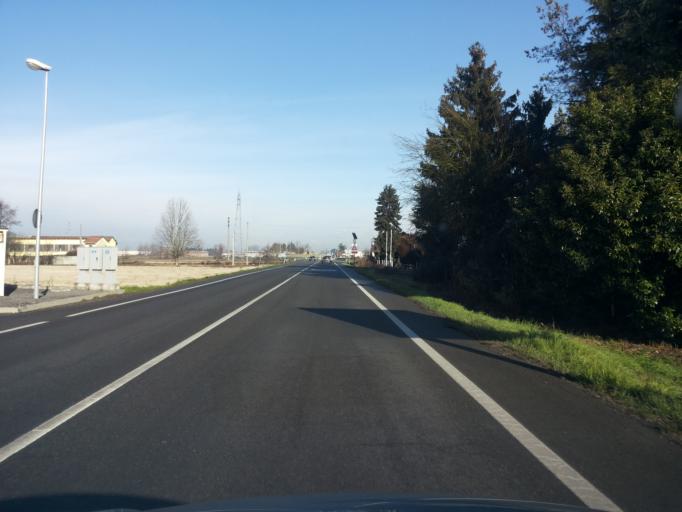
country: IT
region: Piedmont
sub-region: Provincia di Vercelli
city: Caresanablot
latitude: 45.3393
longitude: 8.3934
